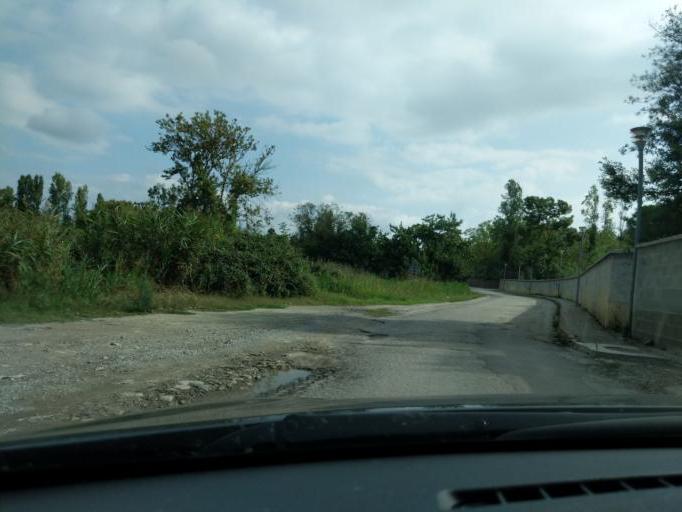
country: FR
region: Corsica
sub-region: Departement de la Haute-Corse
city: Ghisonaccia
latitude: 41.9990
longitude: 9.4423
